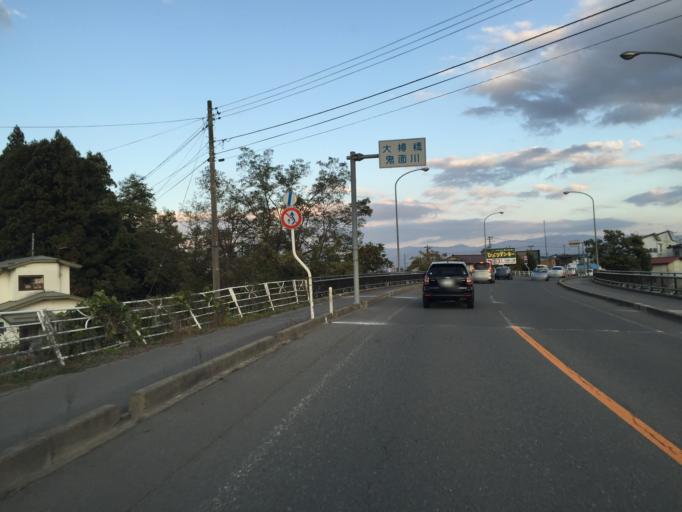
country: JP
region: Yamagata
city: Yonezawa
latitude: 37.9144
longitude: 140.0682
